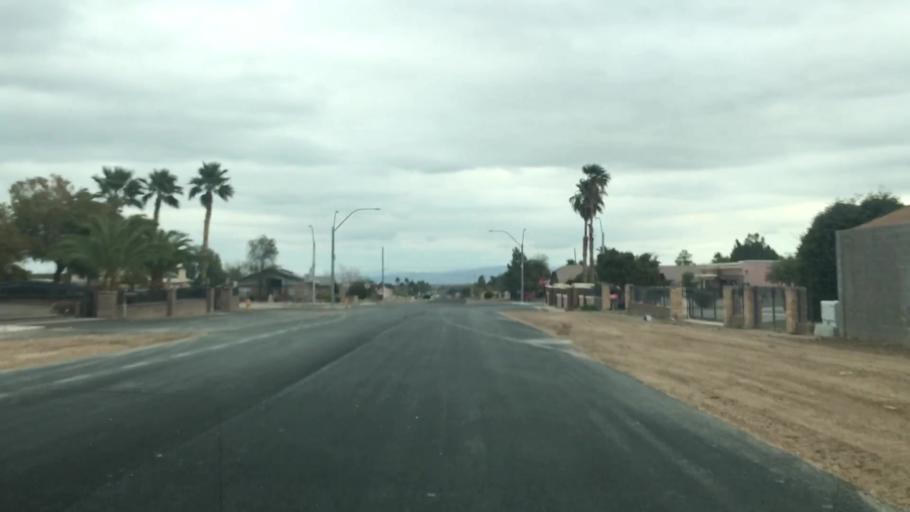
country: US
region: Nevada
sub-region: Clark County
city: Paradise
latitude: 36.0496
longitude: -115.1558
